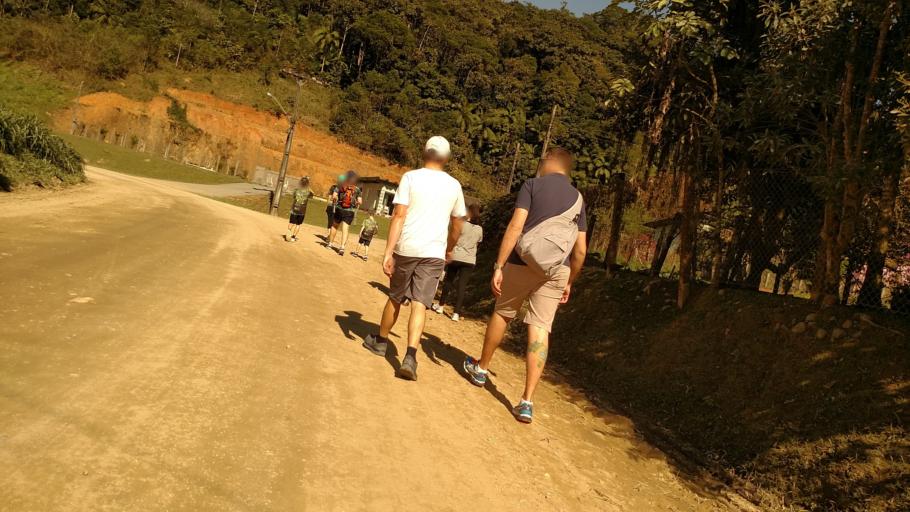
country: BR
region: Santa Catarina
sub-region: Pomerode
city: Pomerode
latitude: -26.7327
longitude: -49.0812
